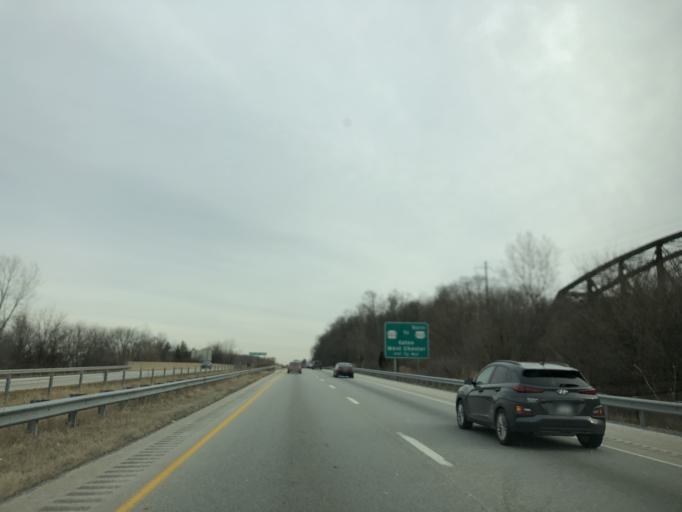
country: US
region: Pennsylvania
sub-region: Chester County
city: Exton
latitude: 40.0149
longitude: -75.6400
